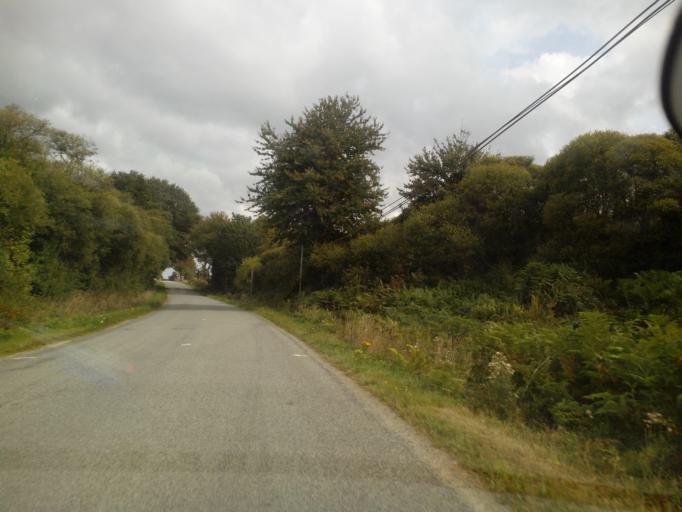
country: FR
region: Brittany
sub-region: Departement du Morbihan
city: Mauron
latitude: 48.1101
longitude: -2.3210
